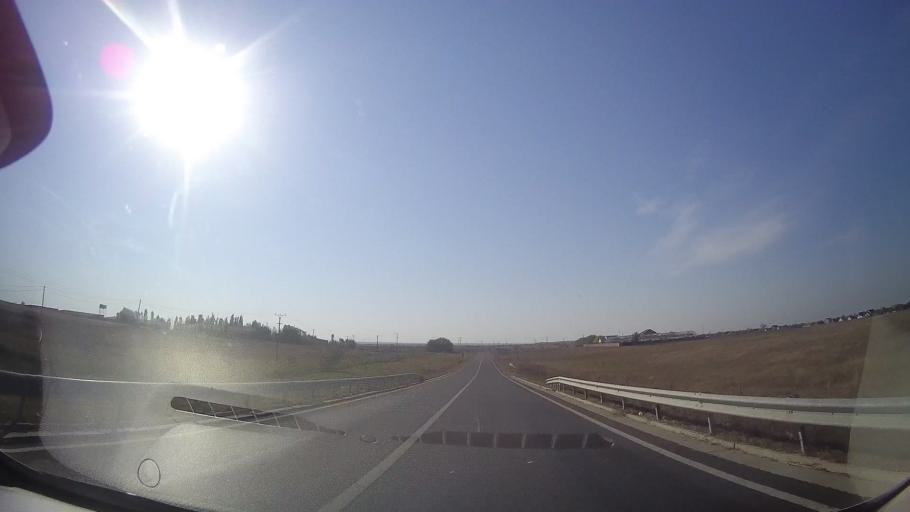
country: RO
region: Timis
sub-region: Oras Recas
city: Recas
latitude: 45.8108
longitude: 21.5285
